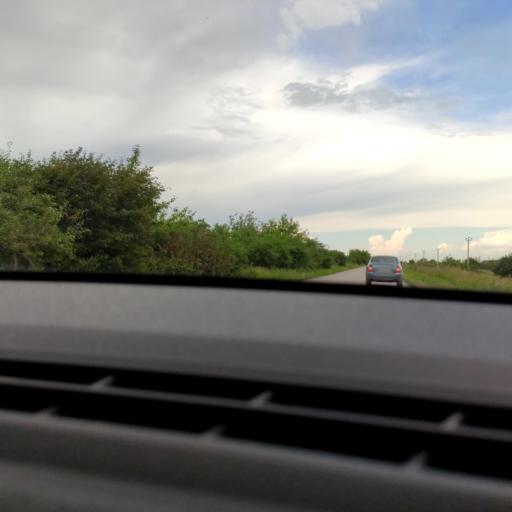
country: RU
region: Samara
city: Podstepki
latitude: 53.5176
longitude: 49.0752
